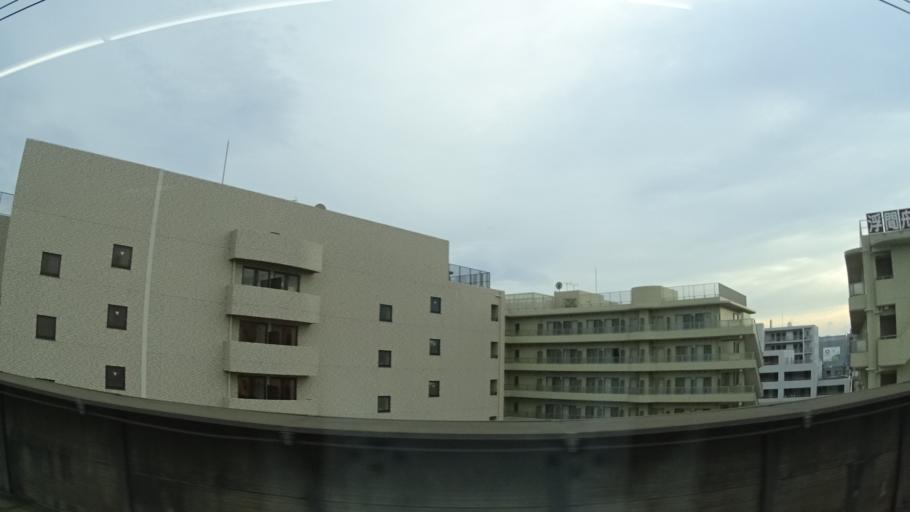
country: JP
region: Saitama
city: Shimotoda
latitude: 35.7936
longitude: 139.6874
